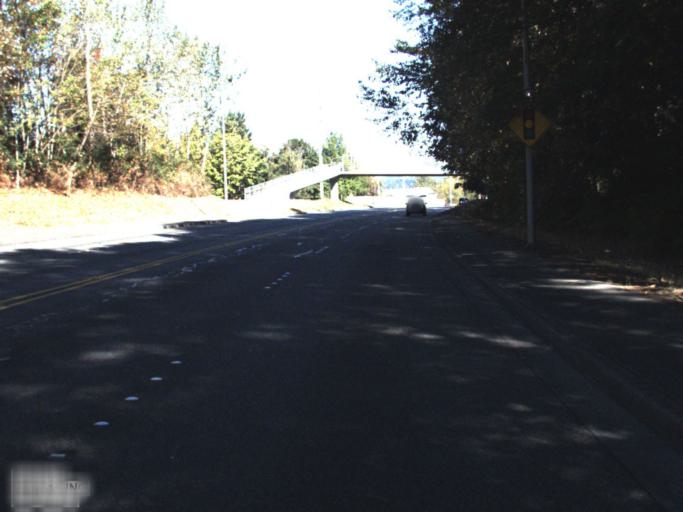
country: US
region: Washington
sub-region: King County
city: Renton
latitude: 47.4579
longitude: -122.2066
